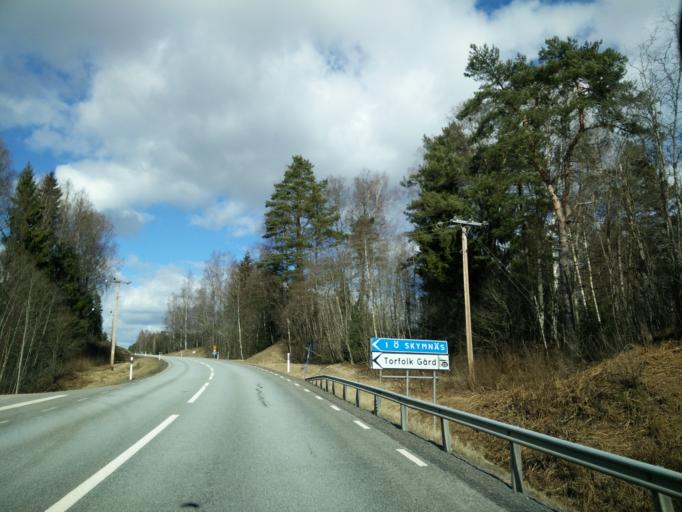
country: SE
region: Vaermland
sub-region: Munkfors Kommun
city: Munkfors
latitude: 59.9134
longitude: 13.5706
